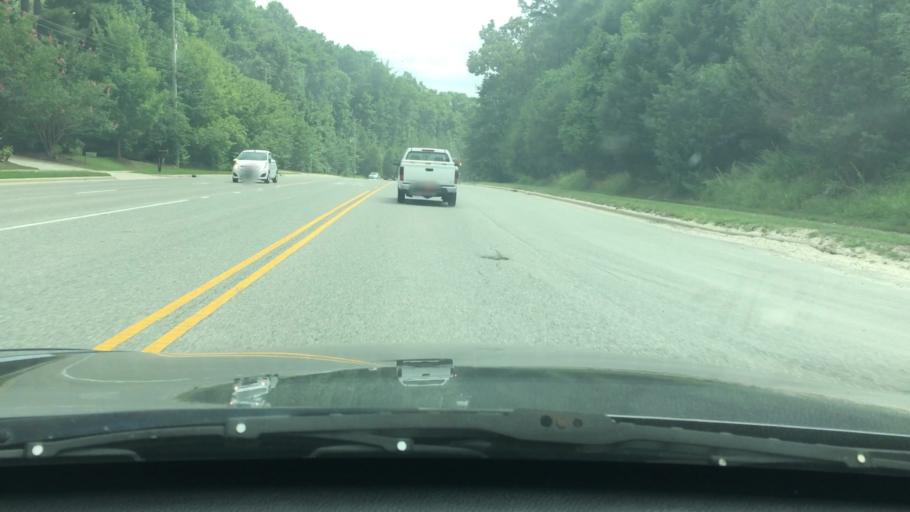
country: US
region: North Carolina
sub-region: Wake County
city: West Raleigh
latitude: 35.8491
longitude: -78.7108
